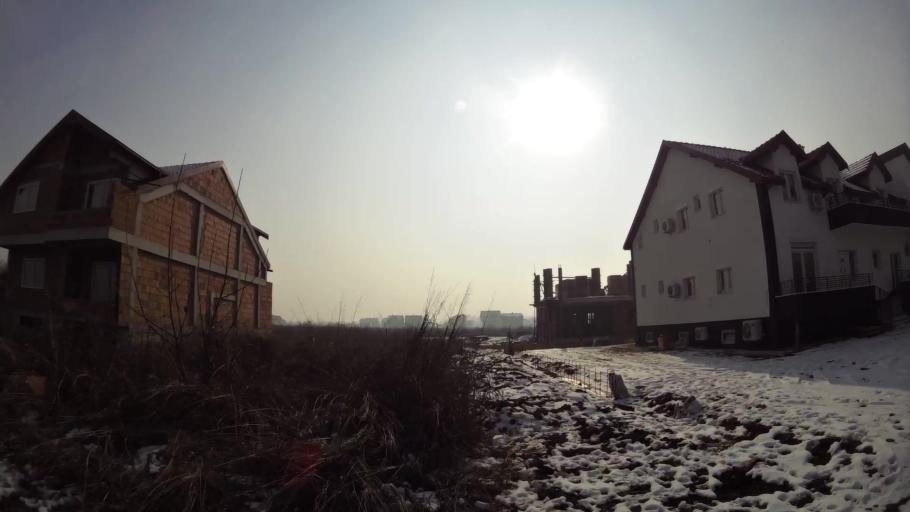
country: MK
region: Kisela Voda
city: Kisela Voda
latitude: 41.9957
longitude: 21.5156
